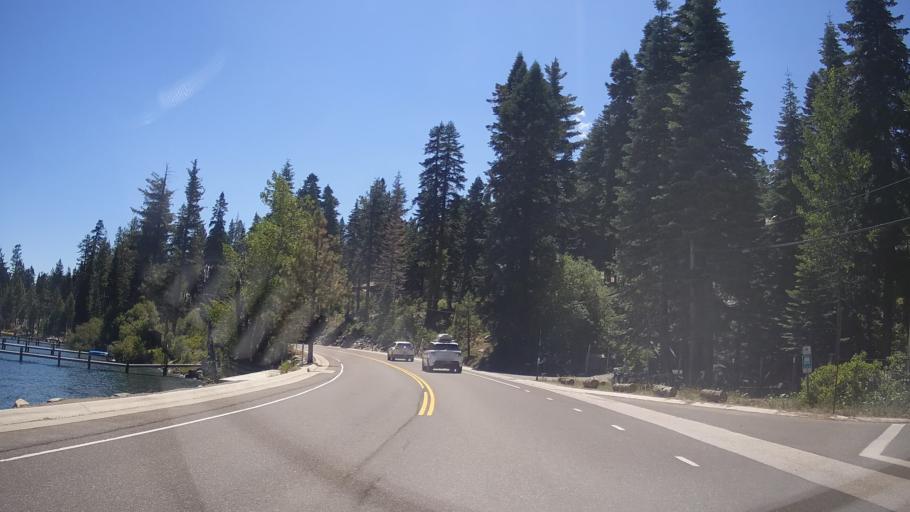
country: US
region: California
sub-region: Placer County
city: Tahoma
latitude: 39.0752
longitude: -120.1510
